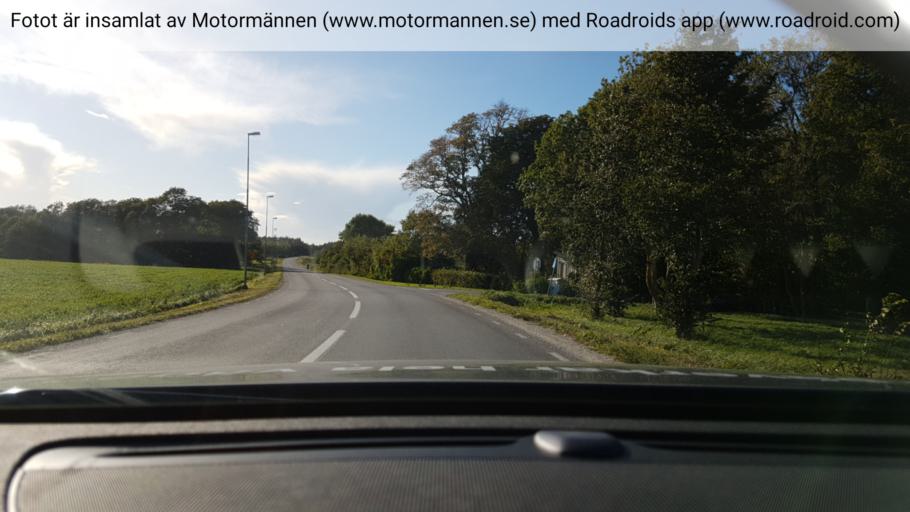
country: SE
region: Gotland
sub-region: Gotland
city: Klintehamn
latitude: 57.3805
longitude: 18.2269
